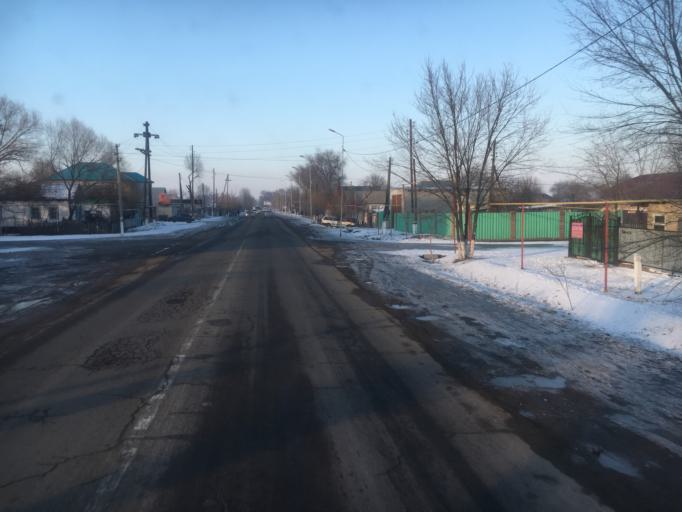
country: KZ
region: Almaty Oblysy
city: Burunday
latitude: 43.3704
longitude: 76.6415
